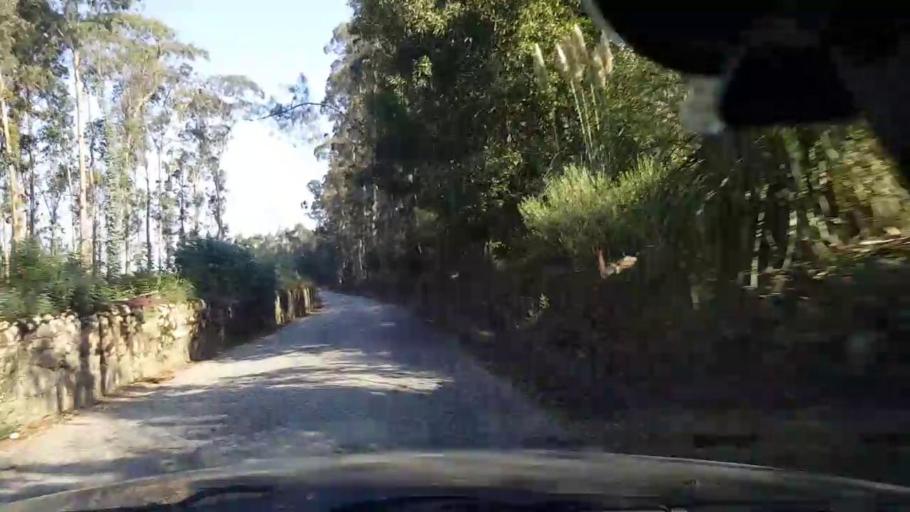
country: PT
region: Porto
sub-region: Vila do Conde
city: Arvore
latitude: 41.3511
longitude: -8.7011
